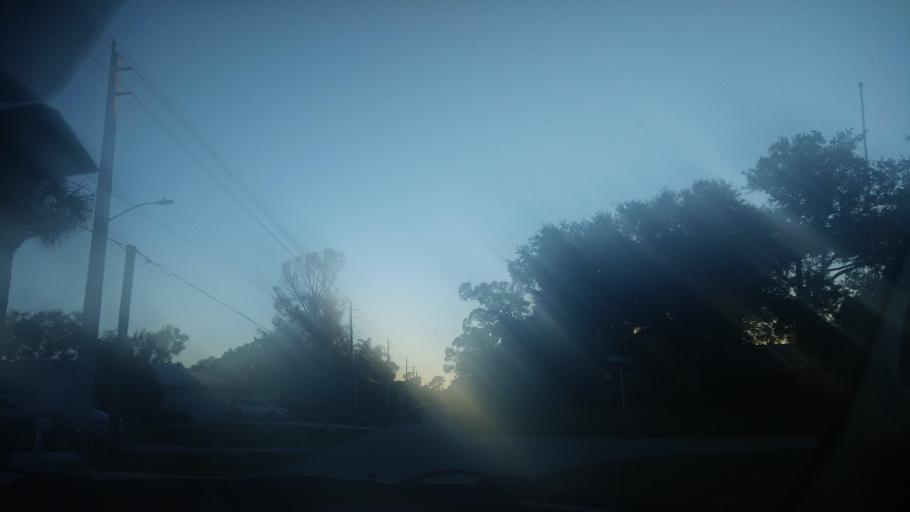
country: US
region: Florida
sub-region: Indian River County
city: Sebastian
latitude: 27.7602
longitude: -80.4838
